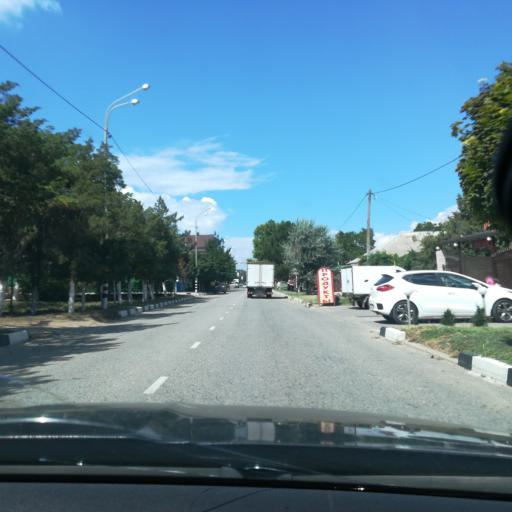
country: RU
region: Krasnodarskiy
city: Taman'
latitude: 45.2174
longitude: 36.7333
